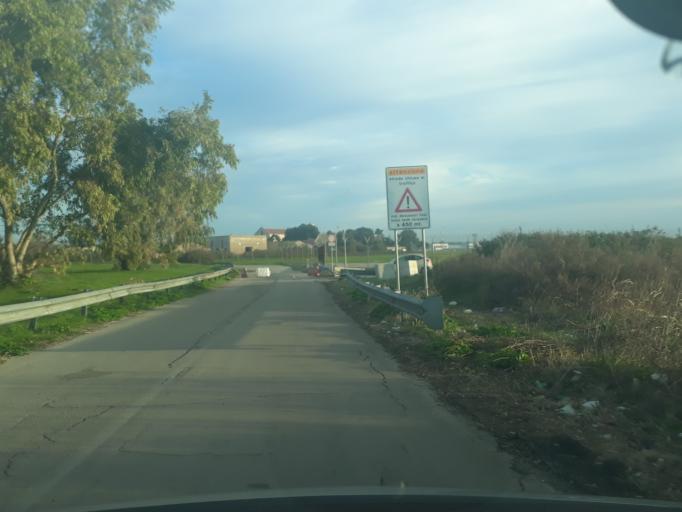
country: IT
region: Apulia
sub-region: Provincia di Brindisi
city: Brindisi
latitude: 40.6505
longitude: 17.9333
